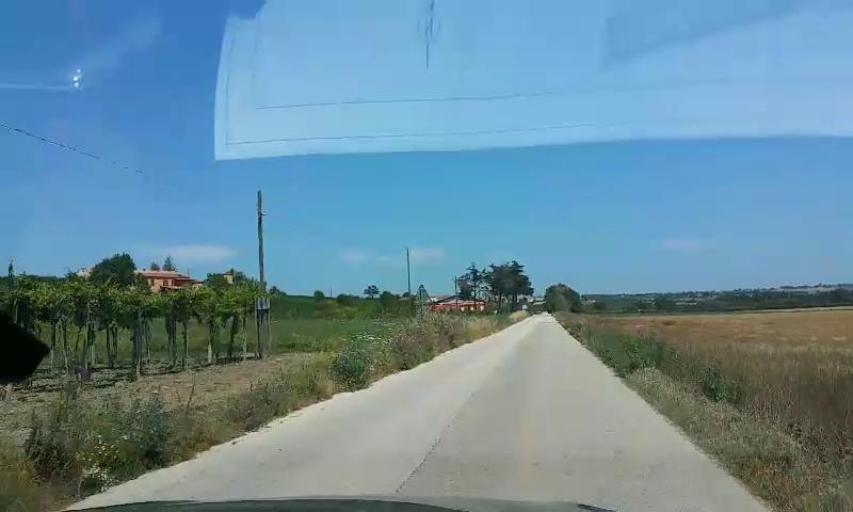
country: IT
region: Molise
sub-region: Provincia di Campobasso
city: San Giacomo degli Schiavoni
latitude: 41.9662
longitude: 14.9005
